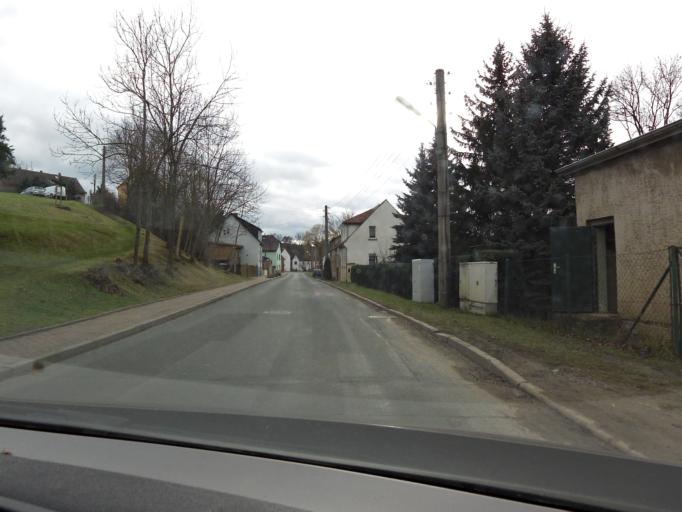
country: DE
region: Thuringia
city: Kapellendorf
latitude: 50.9984
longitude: 11.4819
